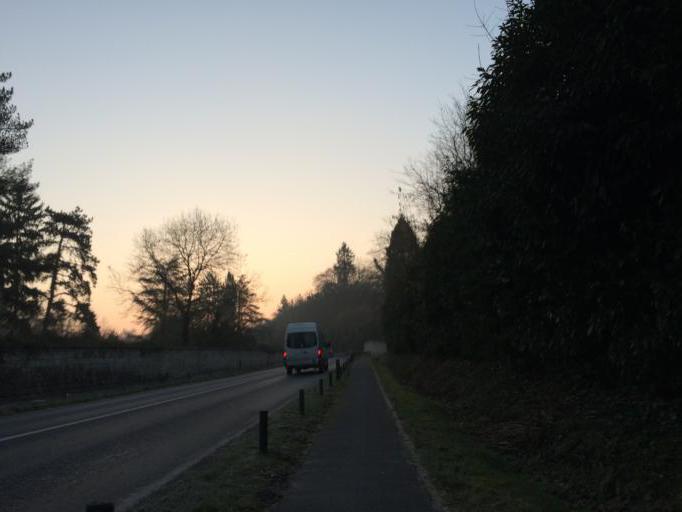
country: FR
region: Picardie
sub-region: Departement de l'Oise
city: Lamorlaye
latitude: 49.1437
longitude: 2.4490
